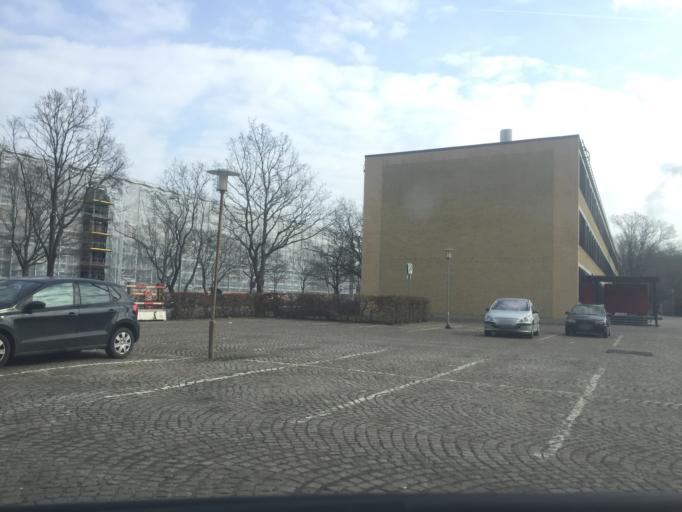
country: DK
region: Capital Region
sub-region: Lyngby-Tarbaek Kommune
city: Kongens Lyngby
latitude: 55.7859
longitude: 12.5184
